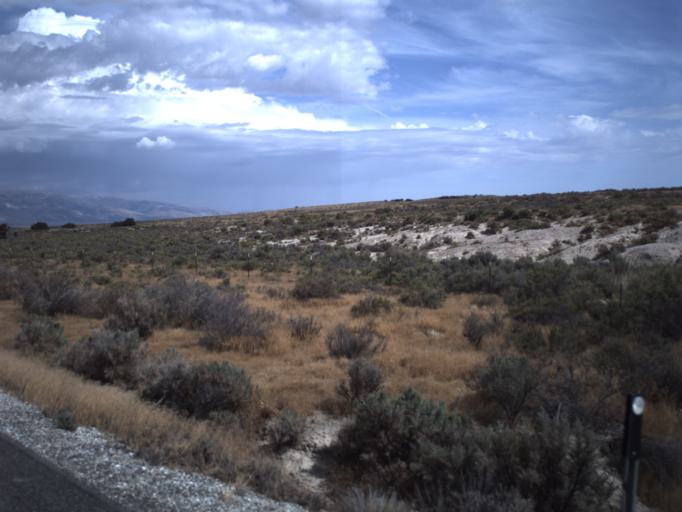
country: US
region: Idaho
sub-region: Cassia County
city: Burley
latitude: 41.6877
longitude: -113.5382
